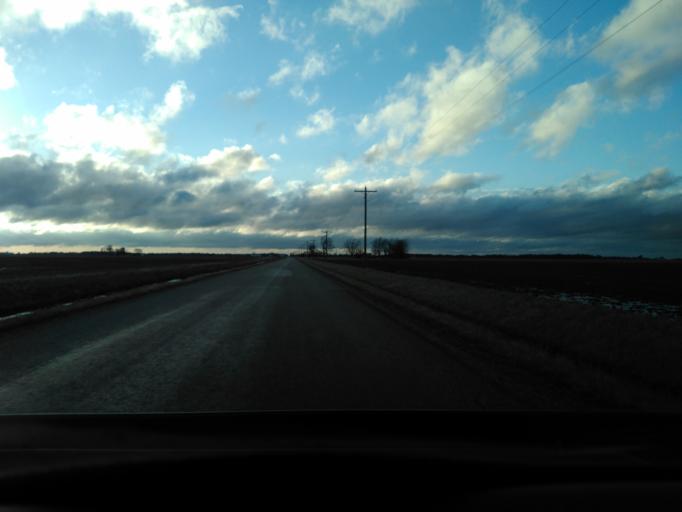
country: US
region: Illinois
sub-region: Effingham County
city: Altamont
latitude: 38.9580
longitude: -88.7178
